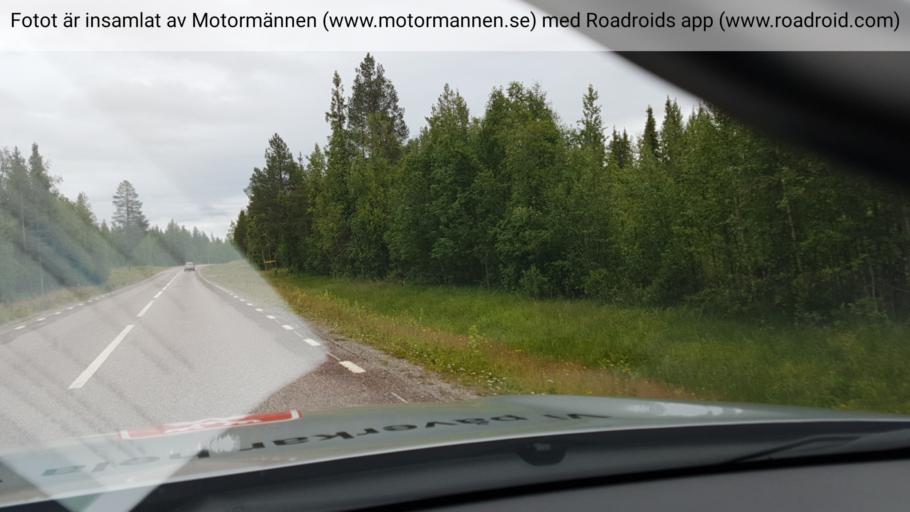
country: SE
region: Norrbotten
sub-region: Gallivare Kommun
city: Gaellivare
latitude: 67.0631
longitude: 21.5698
